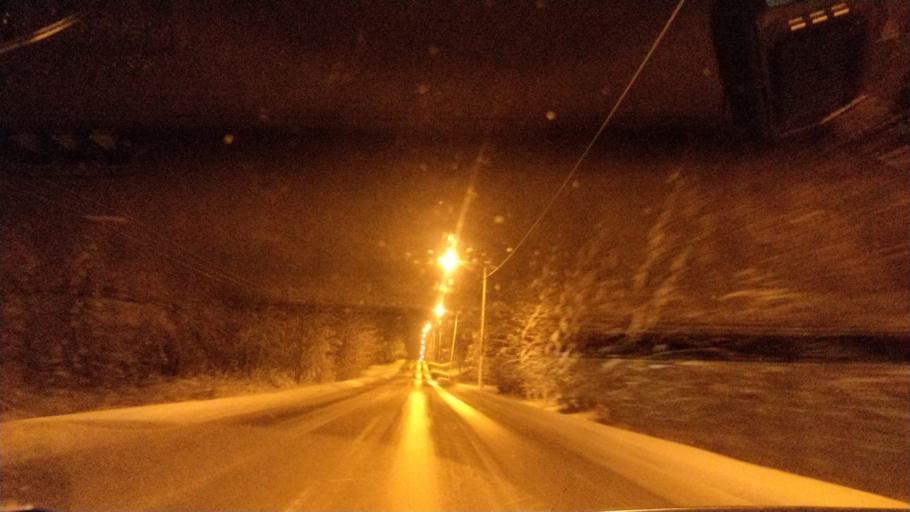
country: FI
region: Lapland
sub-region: Rovaniemi
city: Rovaniemi
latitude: 66.3010
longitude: 25.3538
